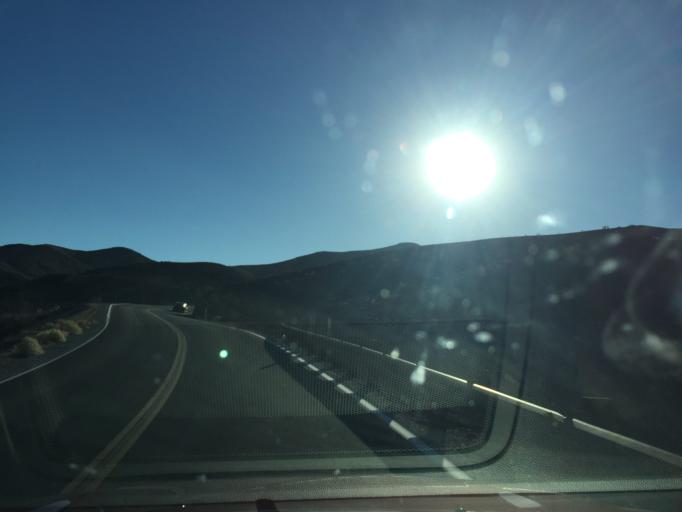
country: US
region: California
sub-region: Inyo County
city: Lone Pine
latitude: 36.3584
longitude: -117.5300
